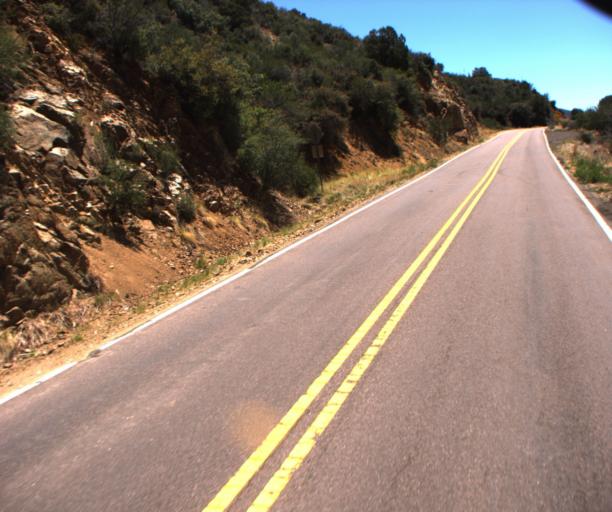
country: US
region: Arizona
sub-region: Yavapai County
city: Prescott
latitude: 34.4586
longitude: -112.5229
